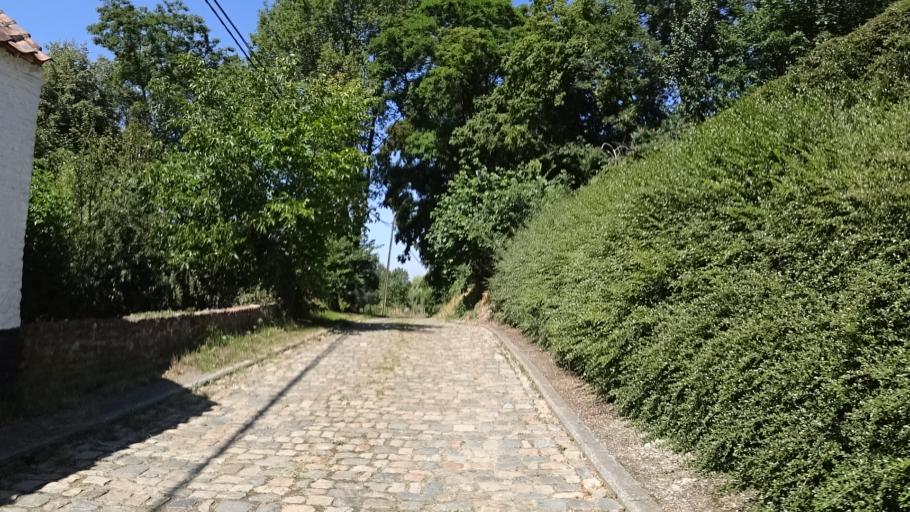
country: BE
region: Wallonia
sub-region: Province du Brabant Wallon
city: Jodoigne
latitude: 50.6888
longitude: 4.8450
